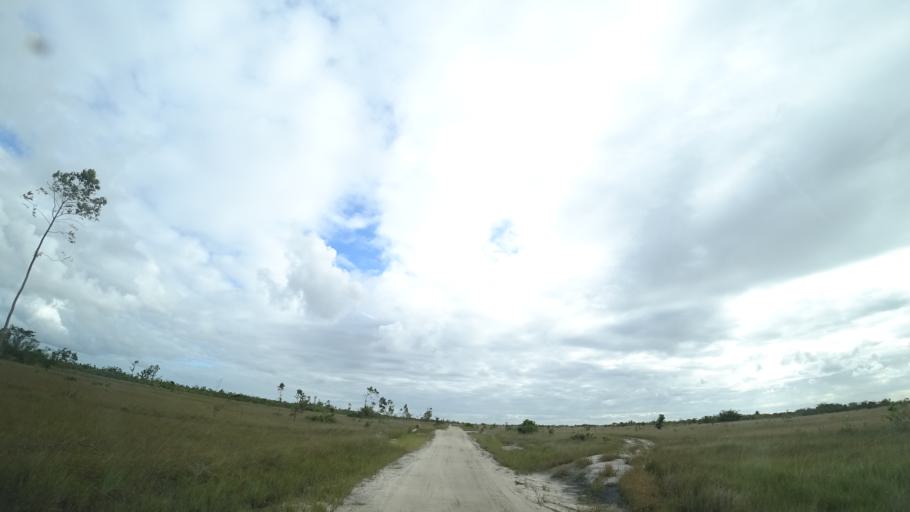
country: MZ
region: Sofala
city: Beira
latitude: -19.6133
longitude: 35.0701
